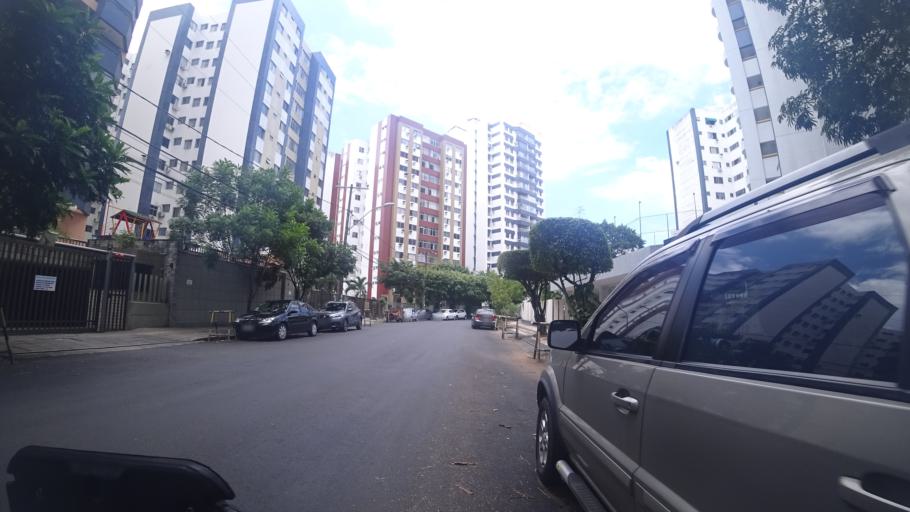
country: BR
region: Bahia
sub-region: Salvador
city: Salvador
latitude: -12.9936
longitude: -38.4723
